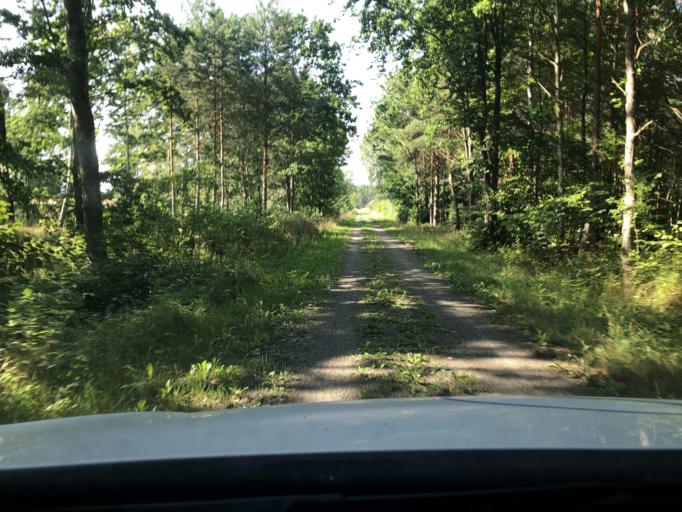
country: SE
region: Skane
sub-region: Kristianstads Kommun
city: Degeberga
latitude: 55.8103
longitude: 14.1322
